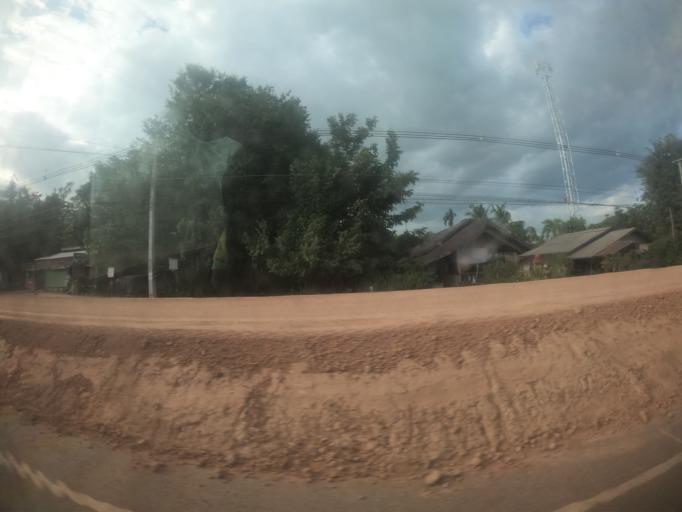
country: TH
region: Surin
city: Kap Choeng
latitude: 14.4667
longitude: 103.6338
